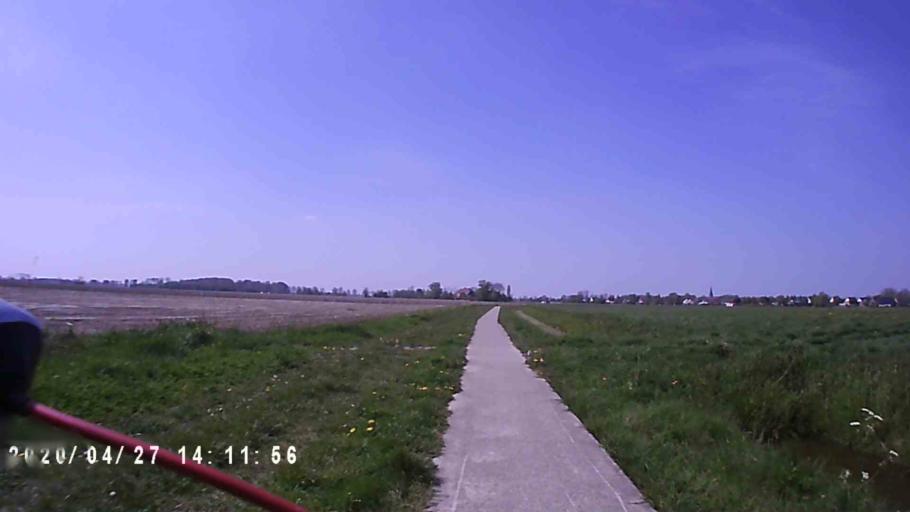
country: NL
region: Groningen
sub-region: Gemeente Zuidhorn
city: Oldehove
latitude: 53.3528
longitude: 6.3888
